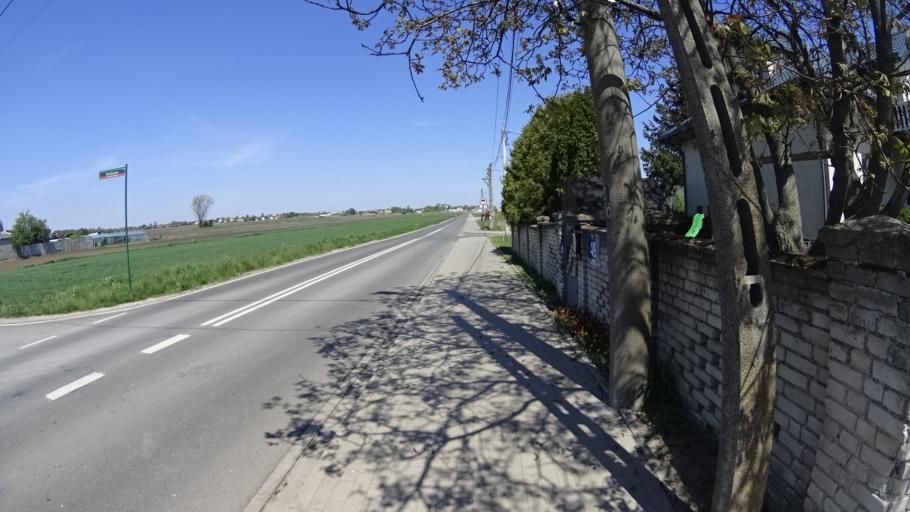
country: PL
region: Masovian Voivodeship
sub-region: Powiat warszawski zachodni
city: Jozefow
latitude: 52.2406
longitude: 20.7378
